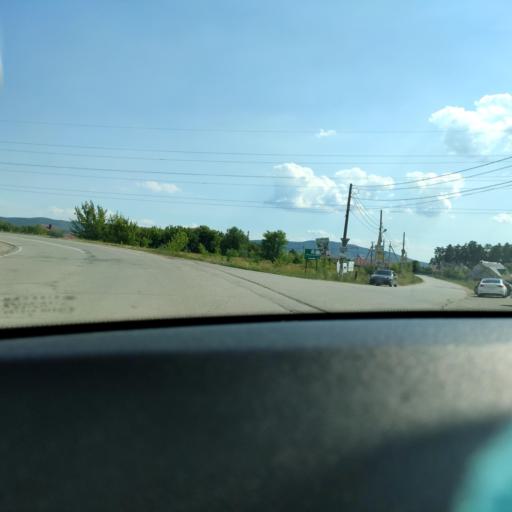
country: RU
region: Samara
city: Volzhskiy
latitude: 53.4471
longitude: 50.1774
